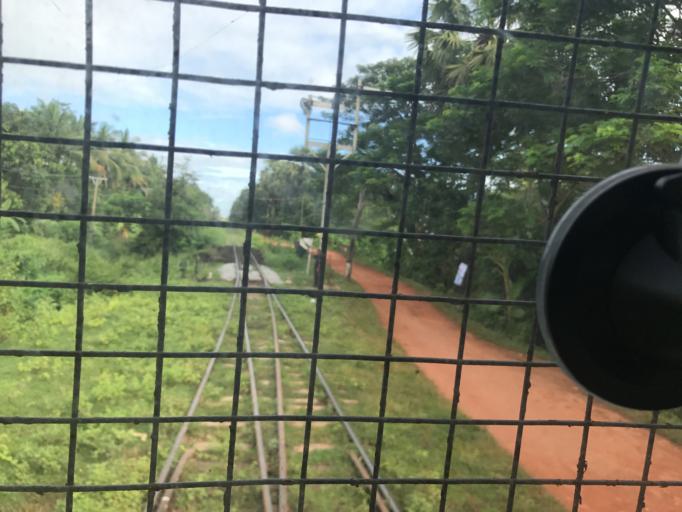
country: MM
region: Bago
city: Letpandan
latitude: 17.8956
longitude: 95.7246
